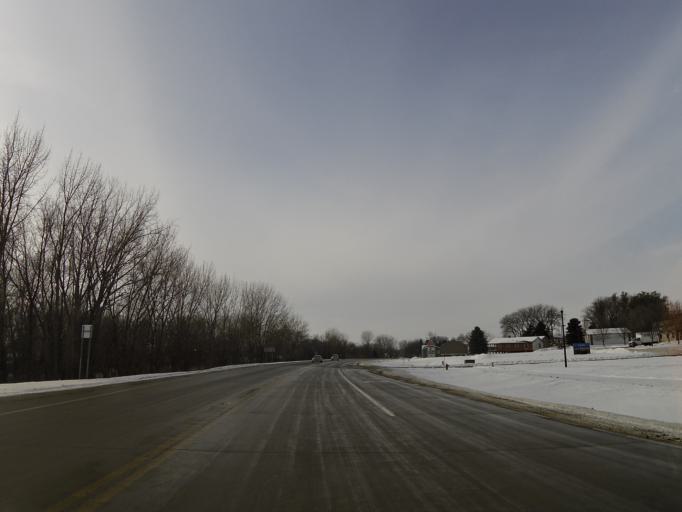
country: US
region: Minnesota
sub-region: McLeod County
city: Hutchinson
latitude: 44.8928
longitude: -94.3990
